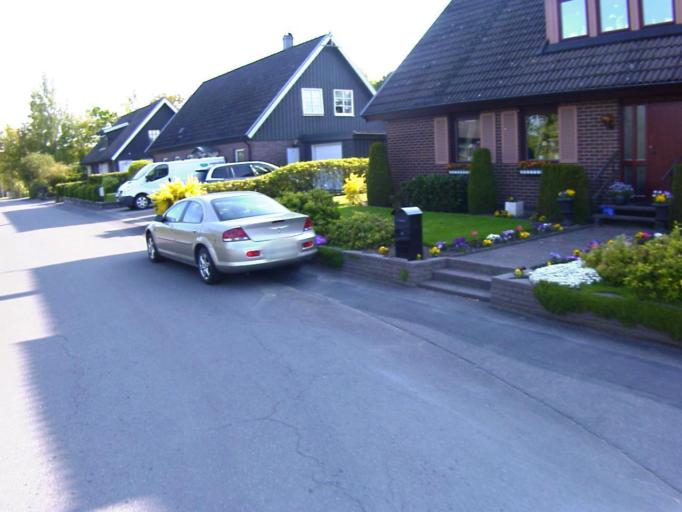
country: SE
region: Skane
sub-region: Kristianstads Kommun
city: Onnestad
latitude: 56.0554
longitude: 14.0258
